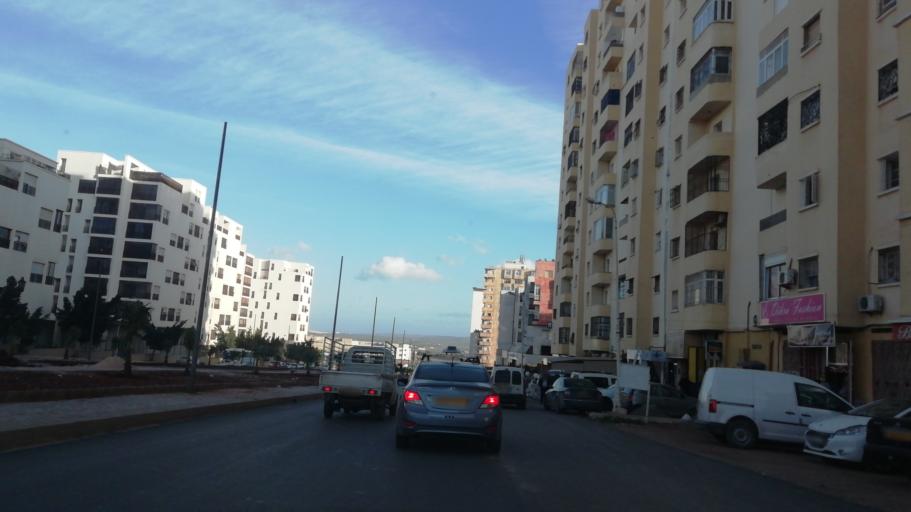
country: DZ
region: Oran
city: Bir el Djir
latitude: 35.7060
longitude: -0.5579
